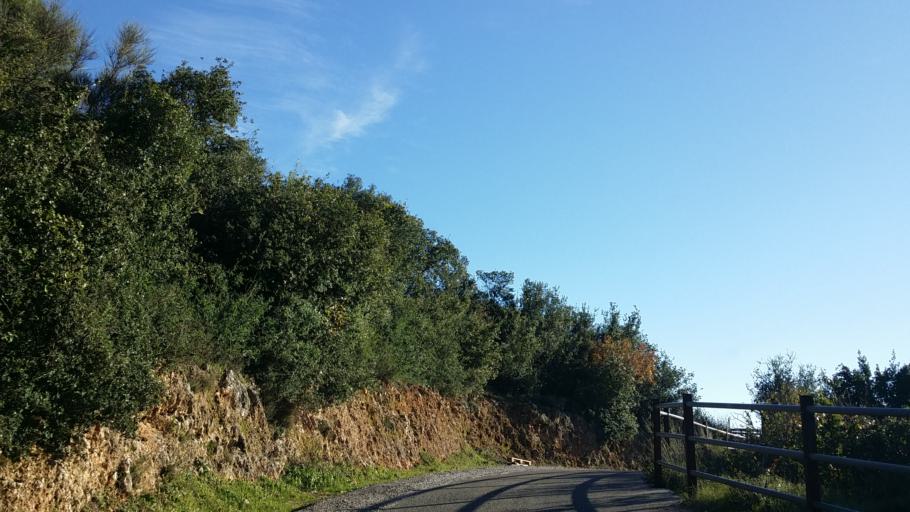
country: GR
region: West Greece
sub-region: Nomos Aitolias kai Akarnanias
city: Fitiai
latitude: 38.7073
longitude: 21.1777
